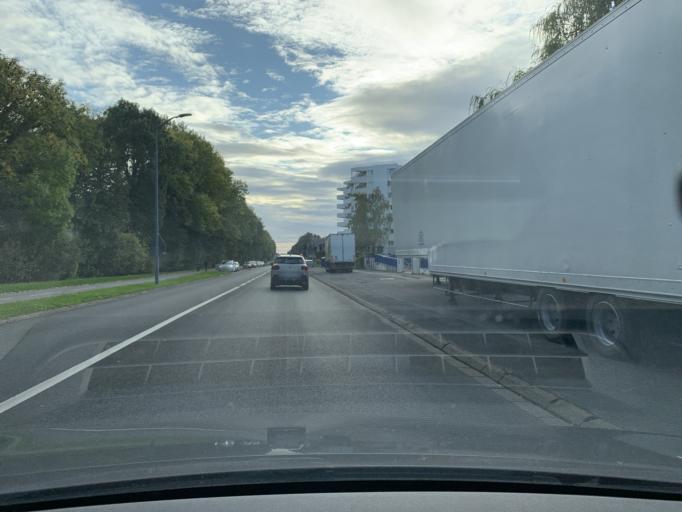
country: FR
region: Picardie
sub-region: Departement de l'Aisne
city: Harly
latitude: 49.8503
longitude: 3.3079
